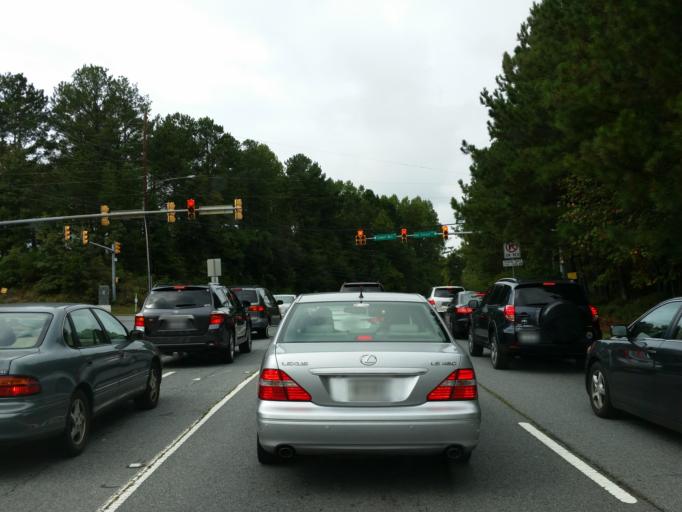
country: US
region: Georgia
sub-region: Fulton County
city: Roswell
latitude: 33.9949
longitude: -84.4336
